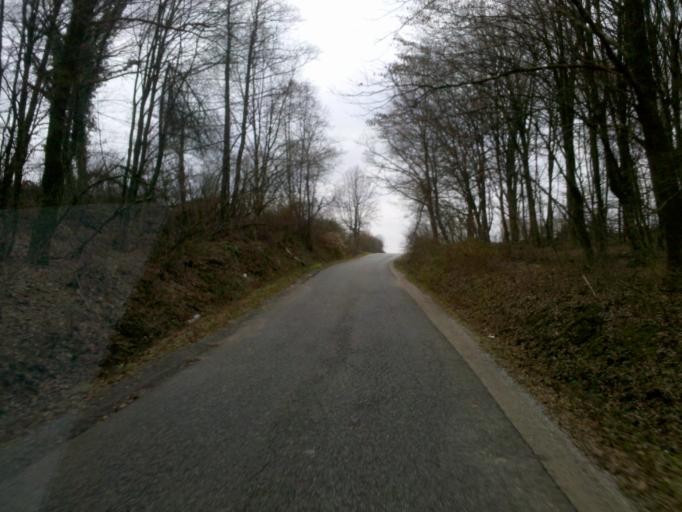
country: HR
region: Grad Zagreb
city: Horvati
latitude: 45.6550
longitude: 15.8037
